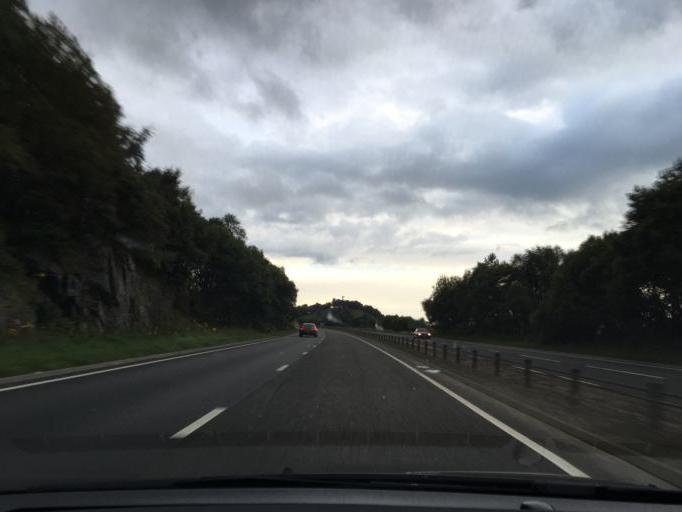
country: GB
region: Scotland
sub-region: Highland
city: Inverness
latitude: 57.4167
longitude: -4.1348
